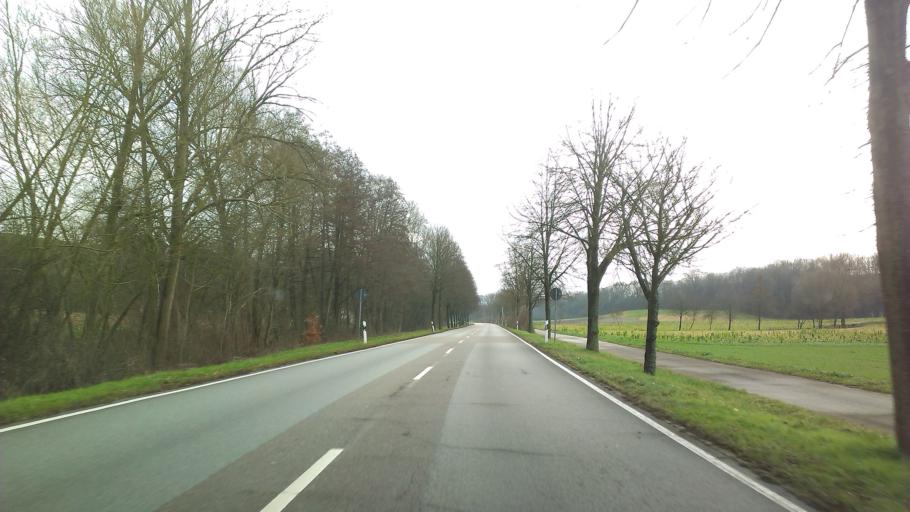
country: DE
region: Baden-Wuerttemberg
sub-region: Karlsruhe Region
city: Balzfeld
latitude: 49.2682
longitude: 8.7944
